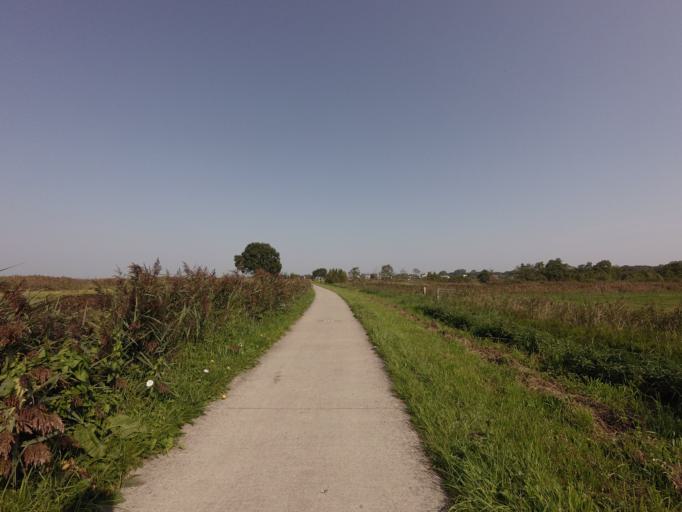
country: NL
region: Groningen
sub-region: Gemeente Groningen
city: Groningen
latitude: 53.1675
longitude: 6.5416
